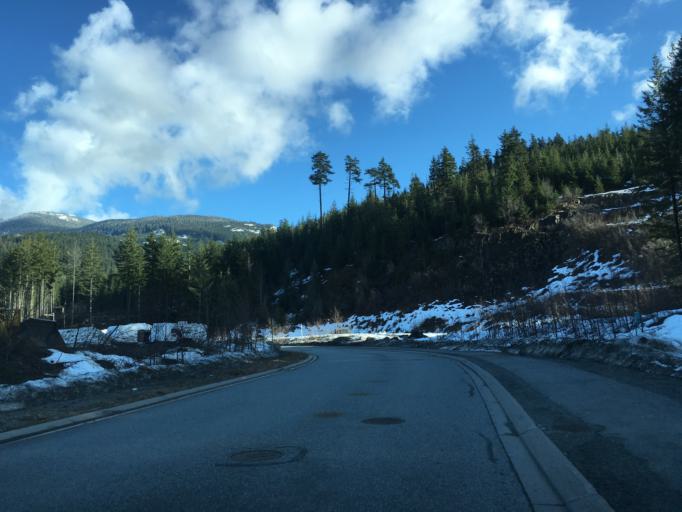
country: CA
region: British Columbia
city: Whistler
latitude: 50.0777
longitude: -123.0450
